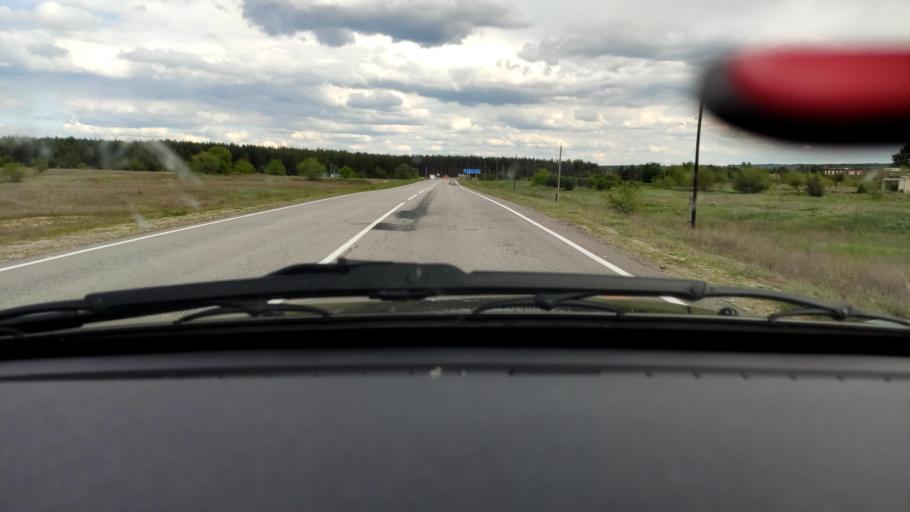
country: RU
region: Voronezj
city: Uryv-Pokrovka
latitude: 51.0510
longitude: 38.9751
